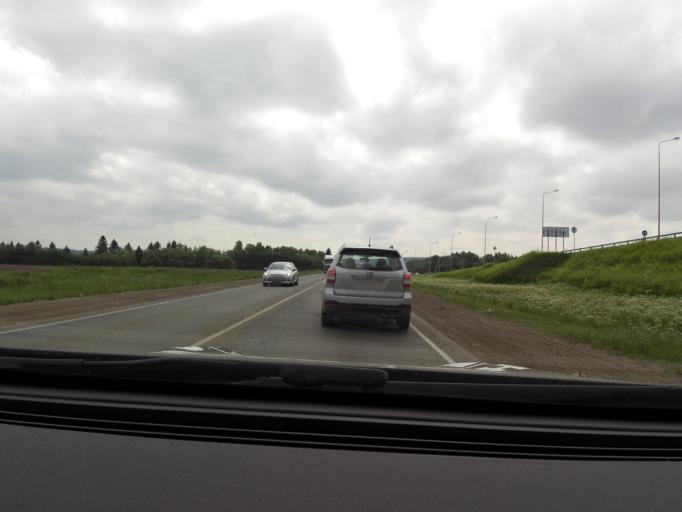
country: RU
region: Perm
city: Zvezdnyy
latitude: 57.7817
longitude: 56.3442
